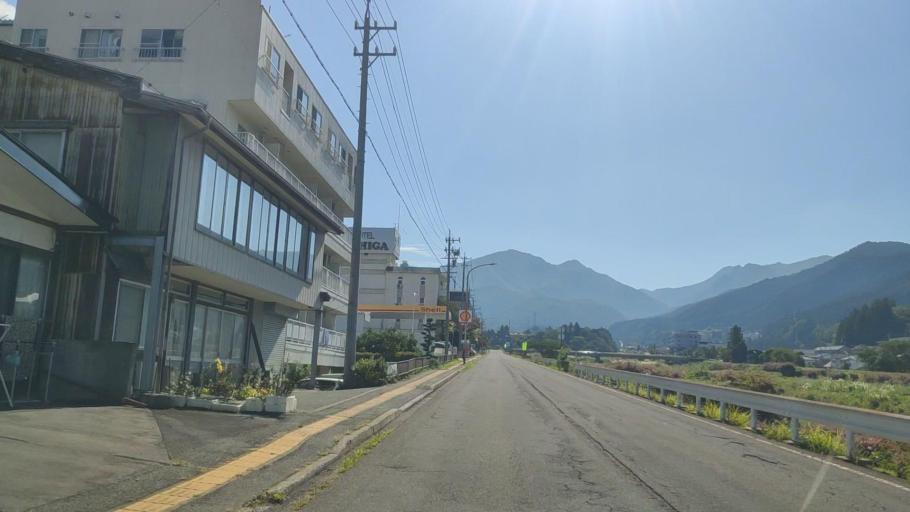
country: JP
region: Nagano
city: Nakano
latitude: 36.7384
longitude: 138.4167
